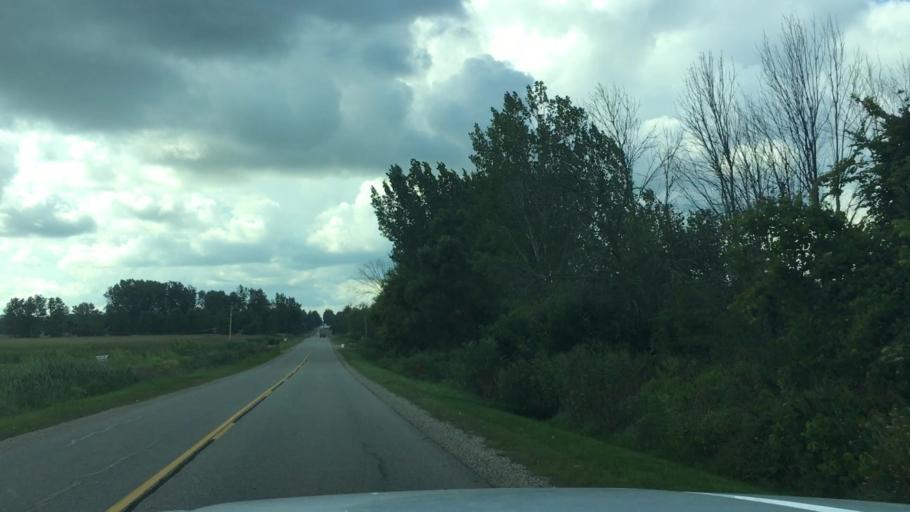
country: US
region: Michigan
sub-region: Ottawa County
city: Hudsonville
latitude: 42.7921
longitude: -85.8418
